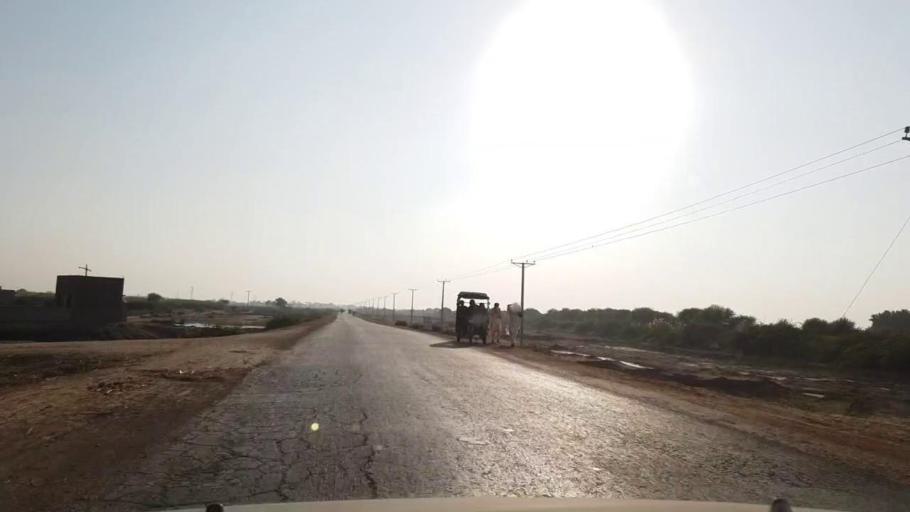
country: PK
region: Sindh
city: Mirpur Batoro
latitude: 24.7567
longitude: 68.2705
